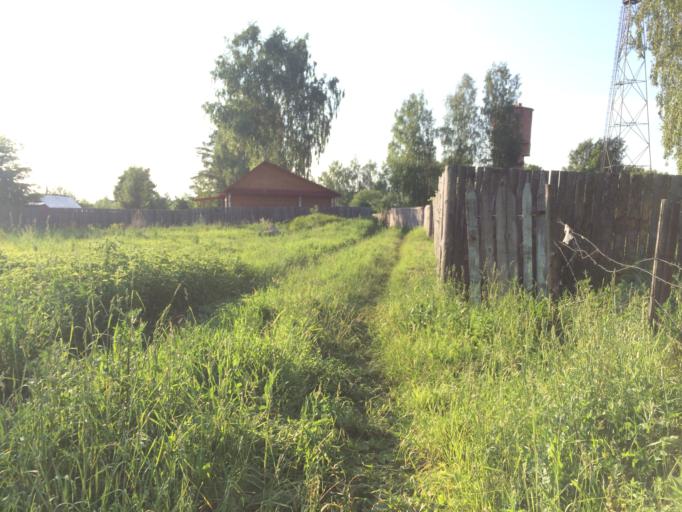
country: RU
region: Mariy-El
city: Mochalishche
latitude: 56.5419
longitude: 48.4092
